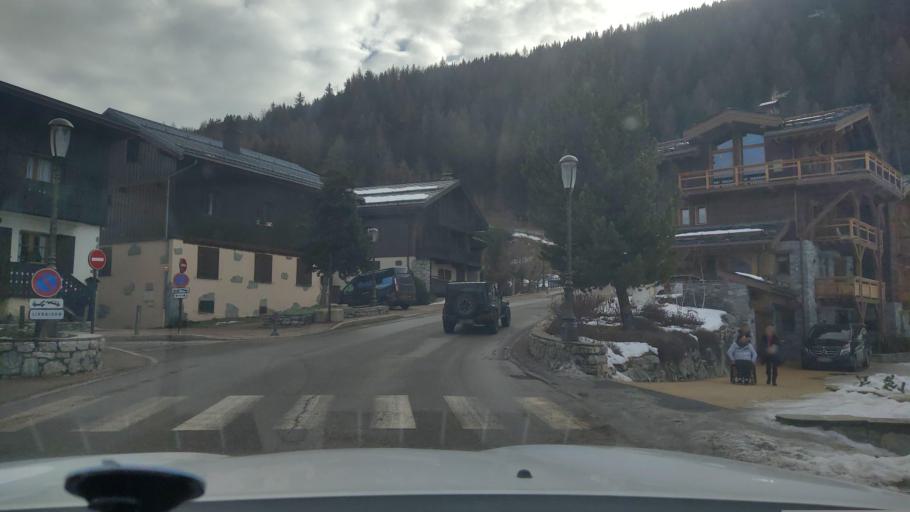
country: FR
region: Rhone-Alpes
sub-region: Departement de la Savoie
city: Saint-Bon-Tarentaise
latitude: 45.4316
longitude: 6.6220
